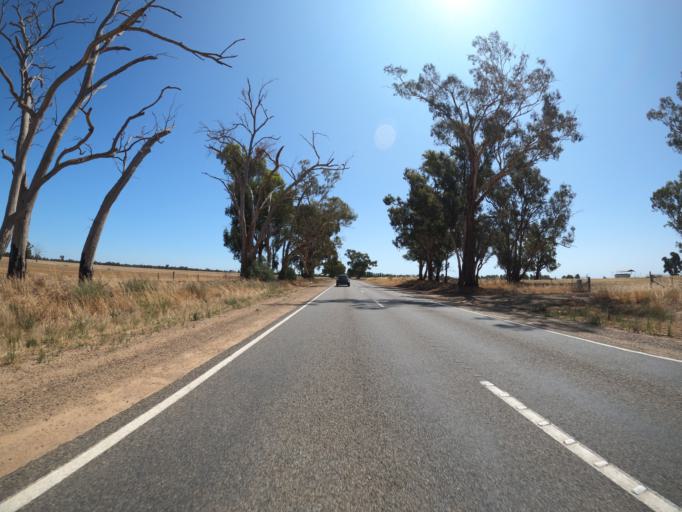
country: AU
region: Victoria
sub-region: Moira
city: Yarrawonga
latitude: -36.0248
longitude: 146.1047
